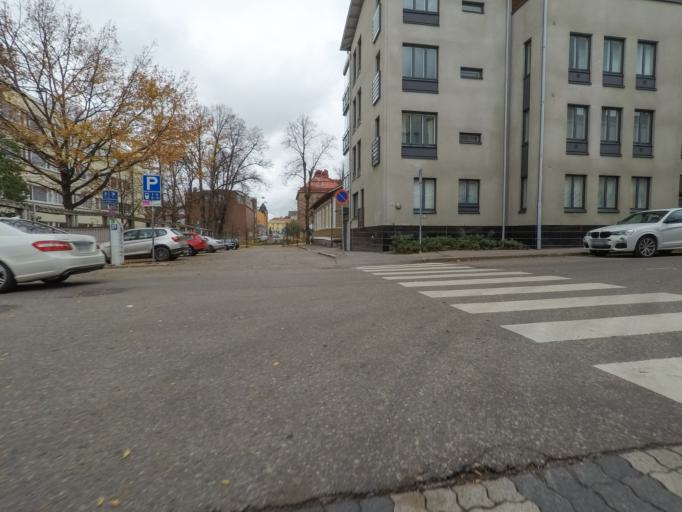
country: FI
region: Uusimaa
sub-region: Porvoo
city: Porvoo
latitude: 60.3917
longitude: 25.6625
